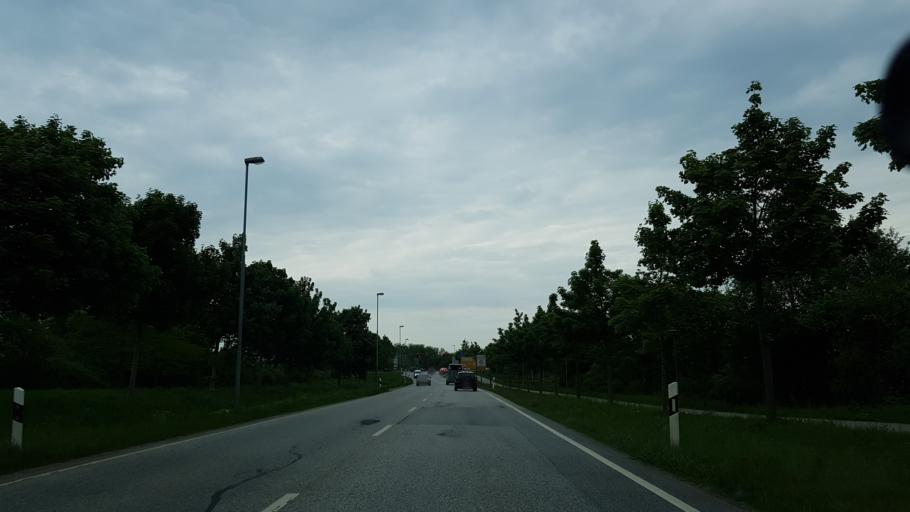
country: DE
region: Schleswig-Holstein
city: Luebeck
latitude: 53.8402
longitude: 10.6557
